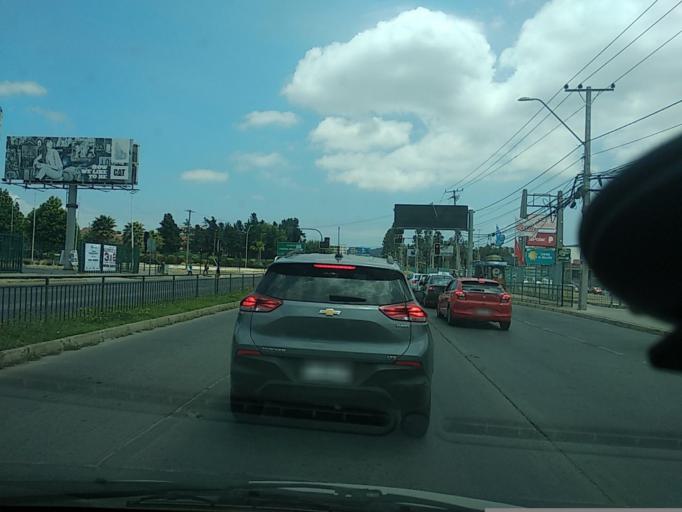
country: CL
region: Valparaiso
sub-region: Provincia de Marga Marga
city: Quilpue
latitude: -33.0437
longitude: -71.4207
